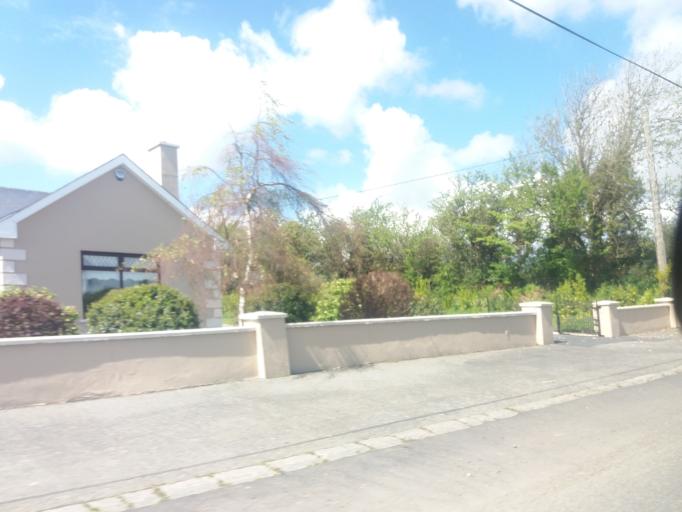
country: IE
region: Munster
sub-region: Waterford
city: Dunmore East
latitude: 52.2439
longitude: -6.8600
